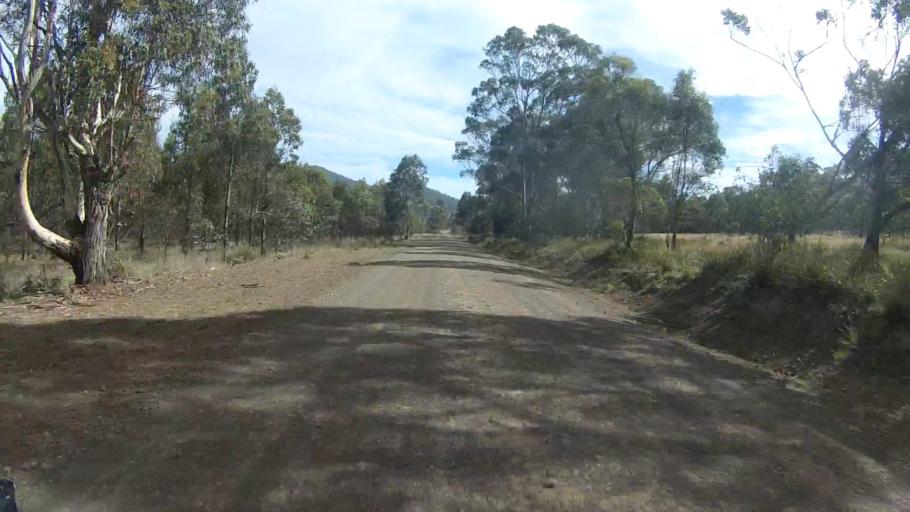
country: AU
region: Tasmania
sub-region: Sorell
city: Sorell
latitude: -42.6556
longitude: 147.8981
